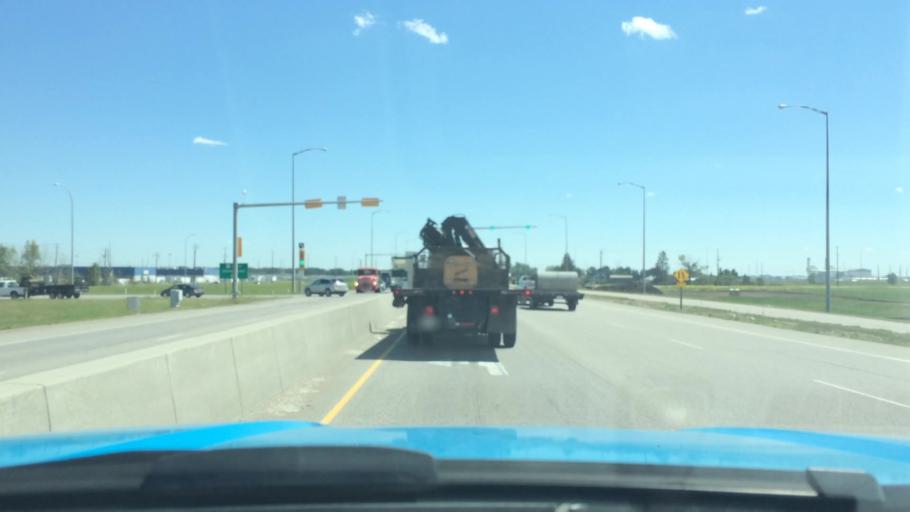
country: CA
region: Alberta
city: Chestermere
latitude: 50.9796
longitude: -113.9163
